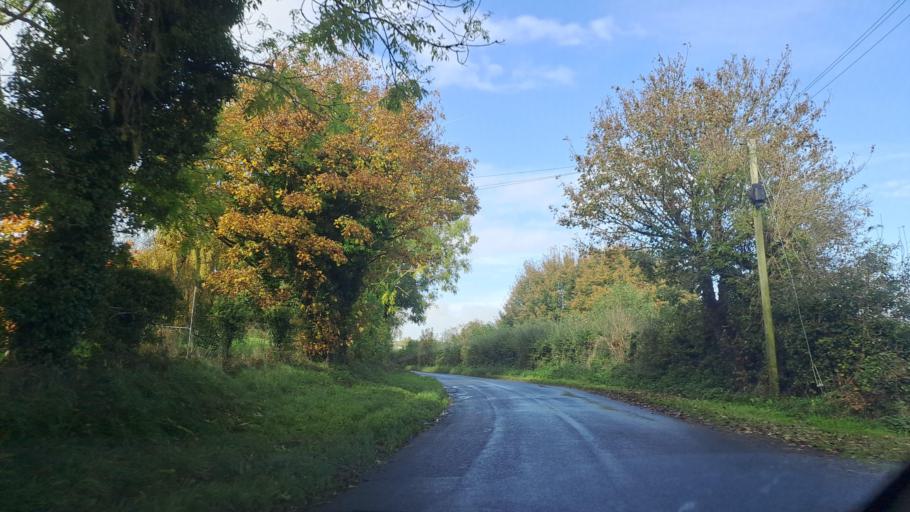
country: IE
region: Leinster
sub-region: Lu
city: Ardee
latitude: 53.8635
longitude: -6.6583
